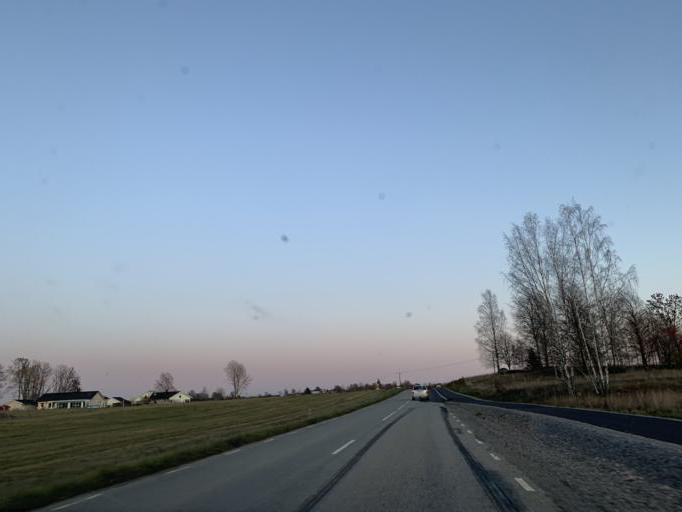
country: SE
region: OErebro
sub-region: Orebro Kommun
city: Hovsta
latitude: 59.3142
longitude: 15.3182
